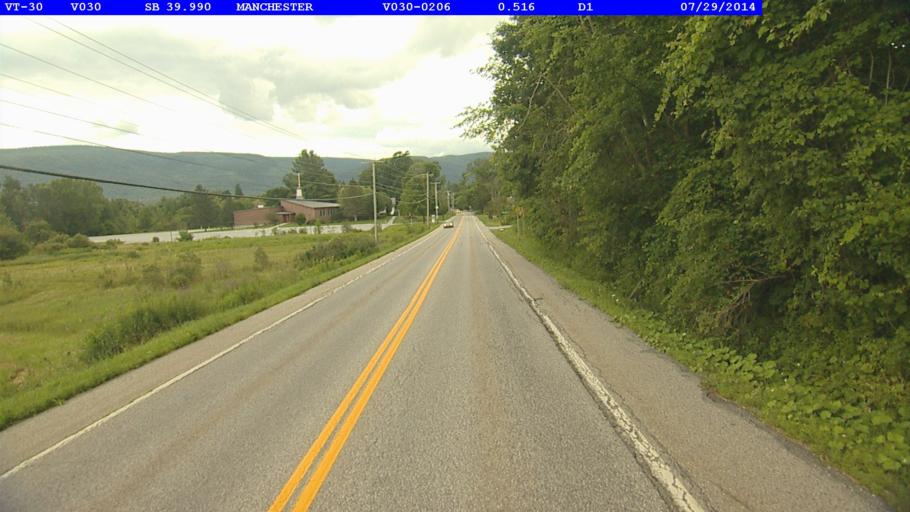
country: US
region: Vermont
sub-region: Bennington County
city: Manchester Center
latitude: 43.1842
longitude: -73.0580
